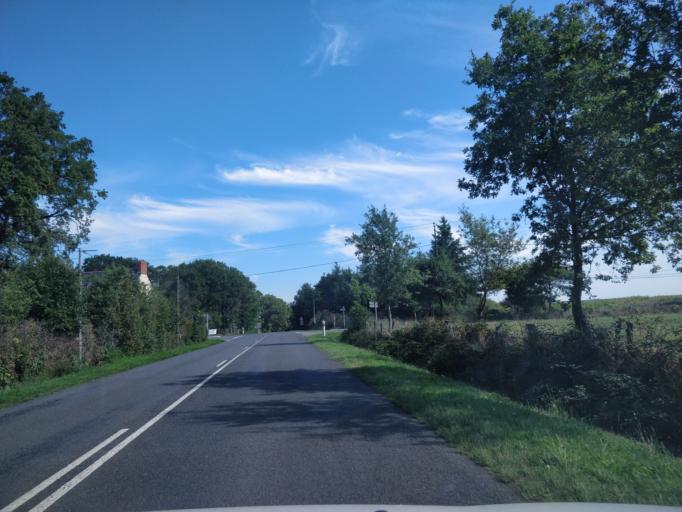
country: FR
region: Pays de la Loire
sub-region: Departement de la Loire-Atlantique
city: Quilly
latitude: 47.4804
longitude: -1.9153
